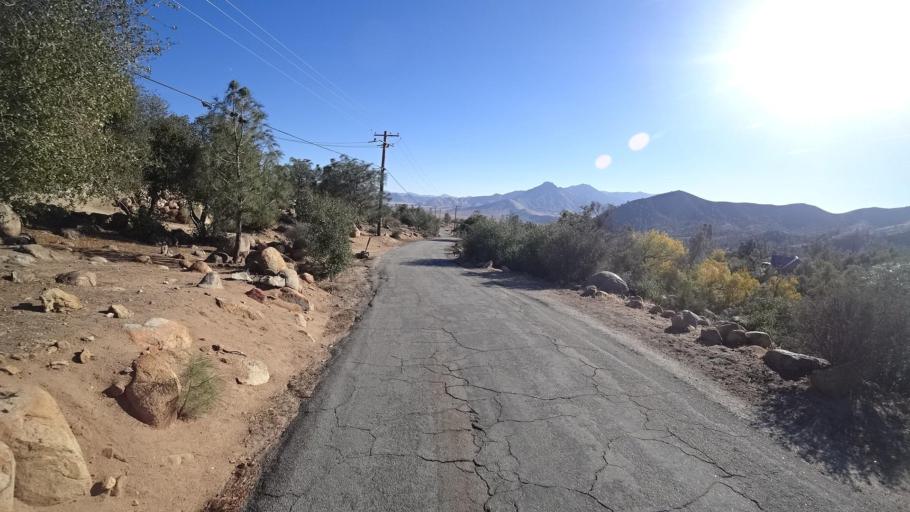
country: US
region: California
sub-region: Kern County
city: Weldon
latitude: 35.7147
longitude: -118.3057
